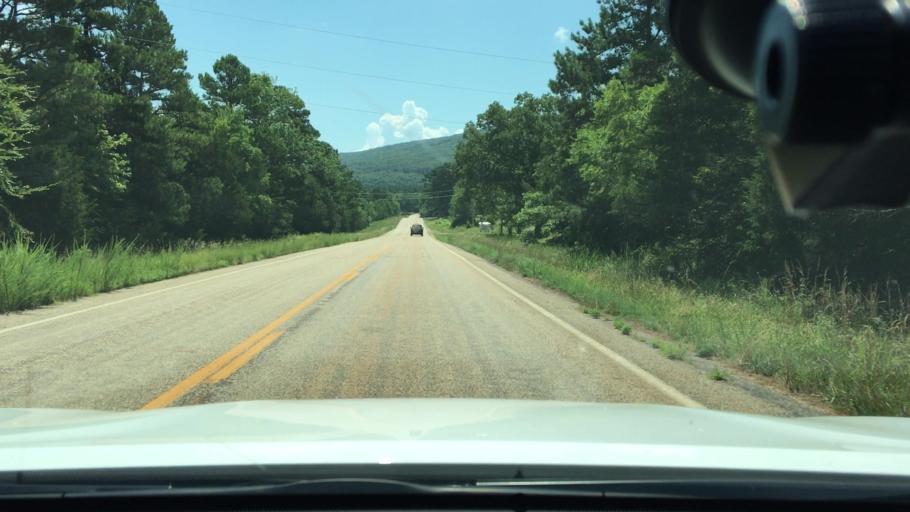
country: US
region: Arkansas
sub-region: Logan County
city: Paris
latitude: 35.1933
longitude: -93.6293
